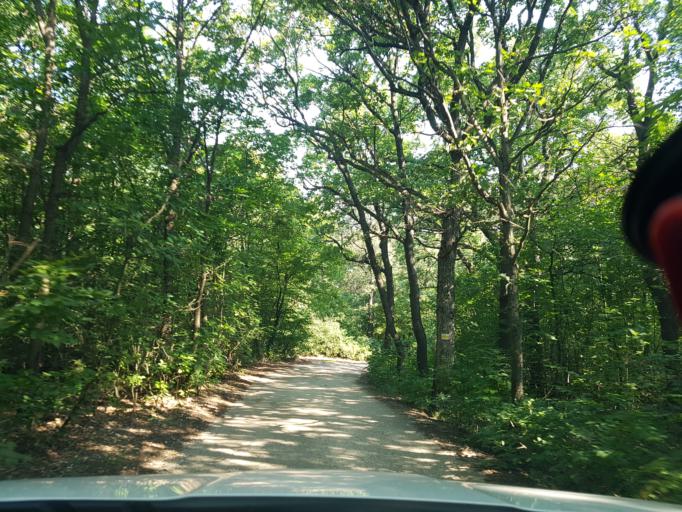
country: HU
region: Veszprem
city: Balatonalmadi
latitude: 47.0058
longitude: 17.9899
